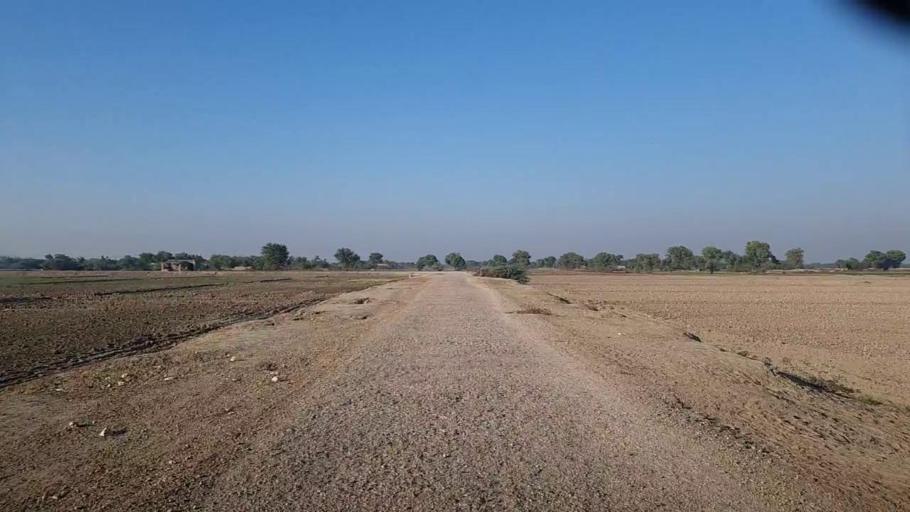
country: PK
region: Sindh
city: Pad Idan
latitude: 26.7326
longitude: 68.3492
